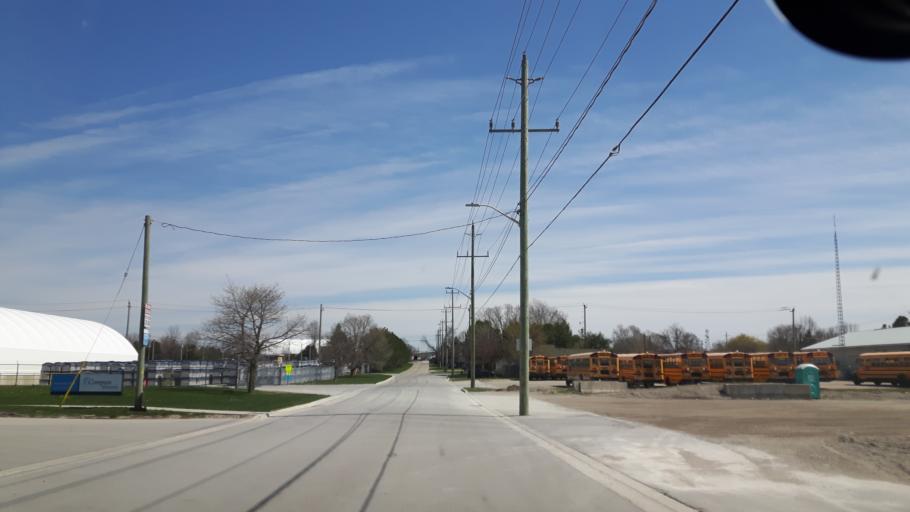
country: CA
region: Ontario
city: Goderich
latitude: 43.7384
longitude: -81.6979
